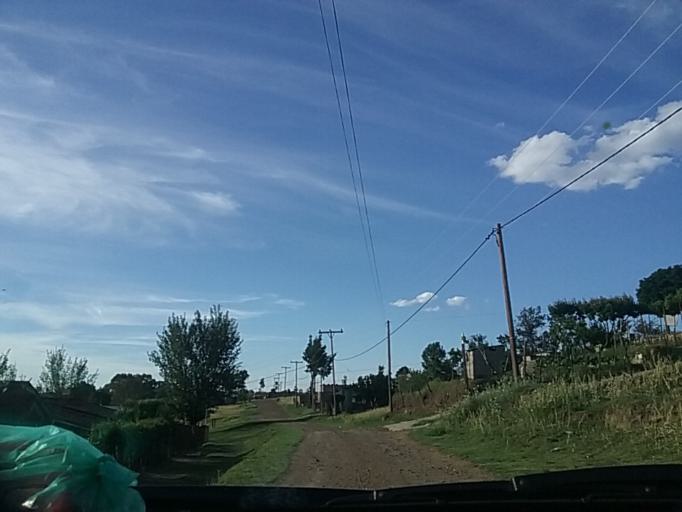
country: LS
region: Berea
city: Teyateyaneng
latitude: -29.1507
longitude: 27.7385
